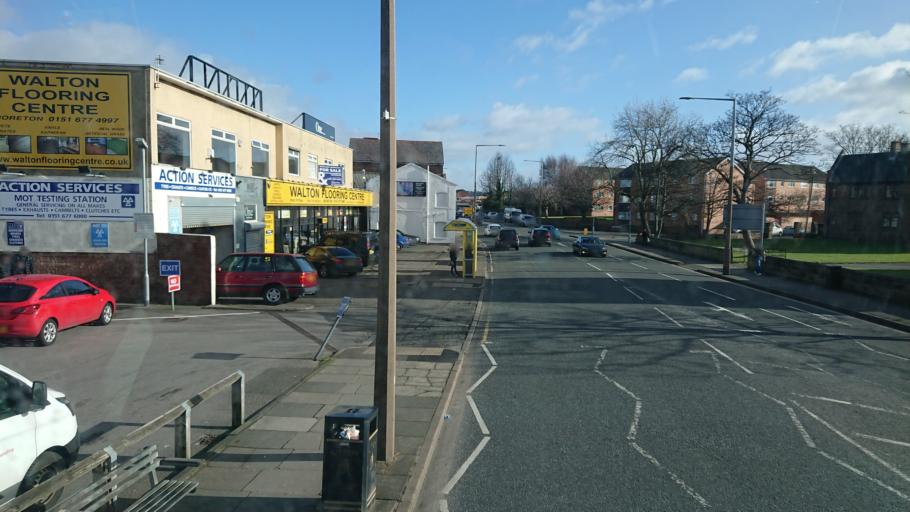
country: GB
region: England
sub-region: Metropolitan Borough of Wirral
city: Moreton
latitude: 53.4013
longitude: -3.1106
